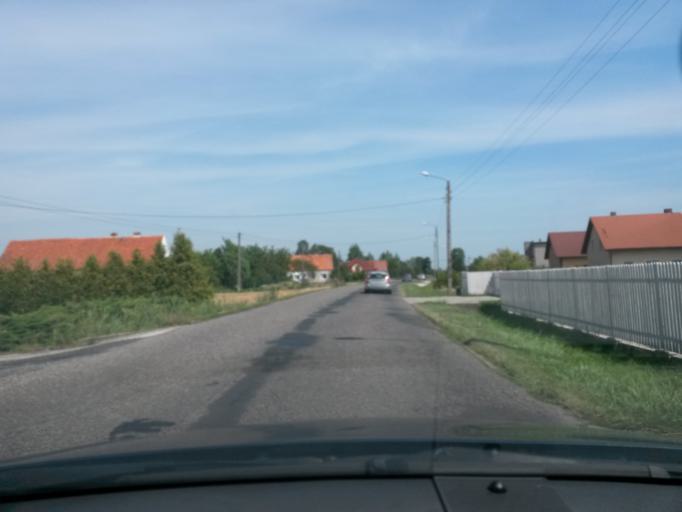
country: PL
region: Lower Silesian Voivodeship
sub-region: Powiat legnicki
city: Prochowice
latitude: 51.2595
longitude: 16.3646
